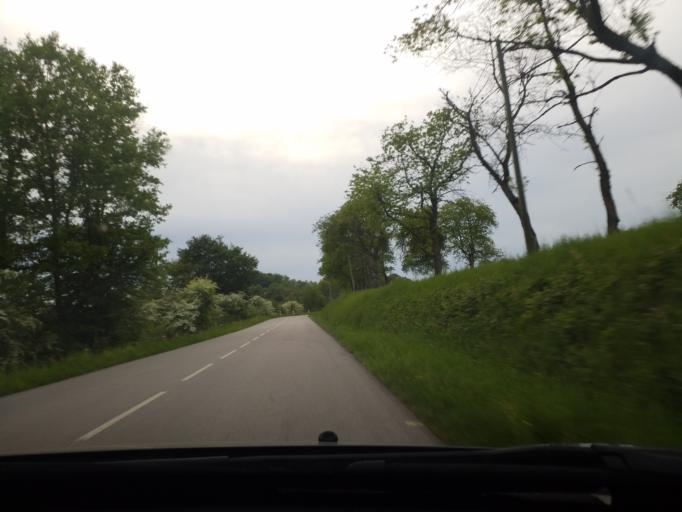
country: FR
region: Lorraine
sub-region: Departement des Vosges
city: Bains-les-Bains
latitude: 48.0321
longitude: 6.1912
